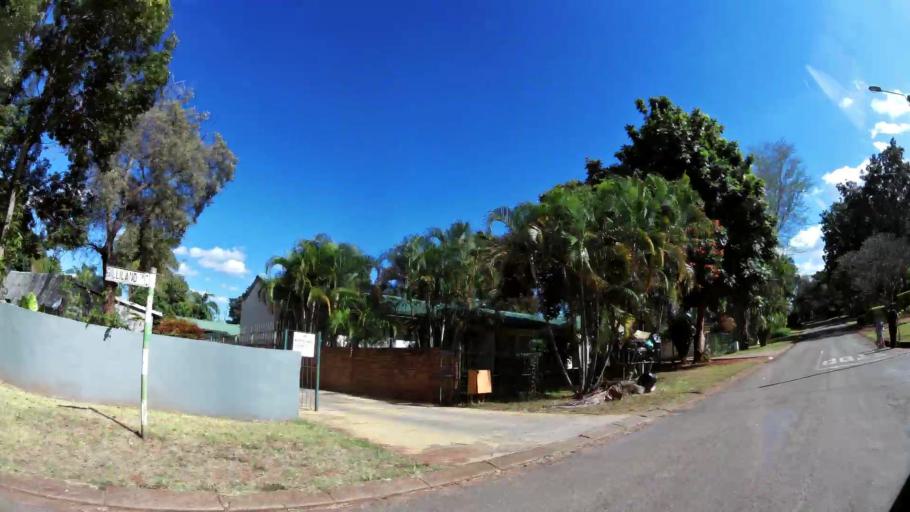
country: ZA
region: Limpopo
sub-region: Mopani District Municipality
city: Tzaneen
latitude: -23.8150
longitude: 30.1563
